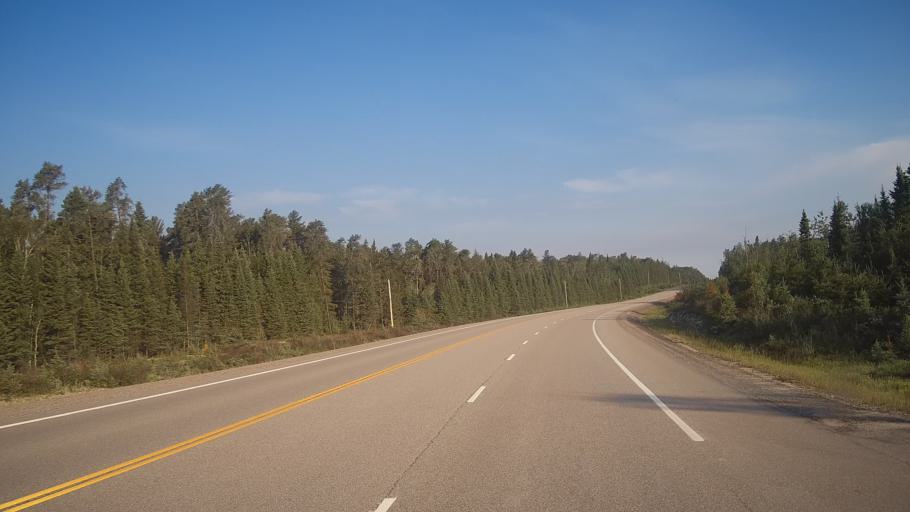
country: CA
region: Ontario
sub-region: Rainy River District
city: Atikokan
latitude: 49.3723
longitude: -91.5713
